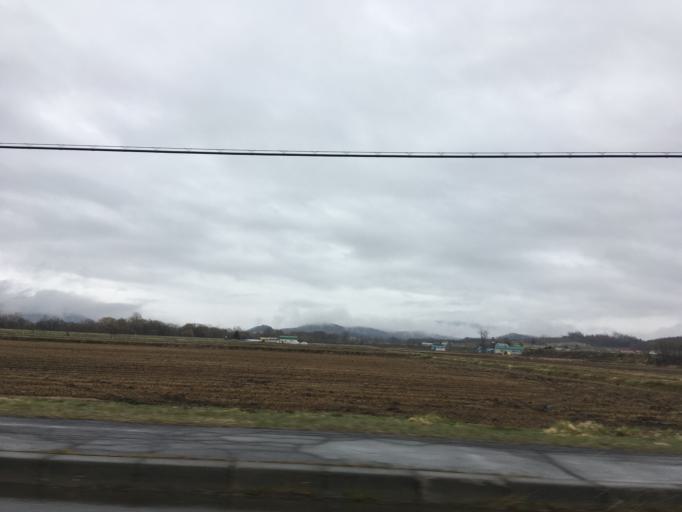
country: JP
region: Hokkaido
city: Nayoro
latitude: 44.1247
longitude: 142.4835
